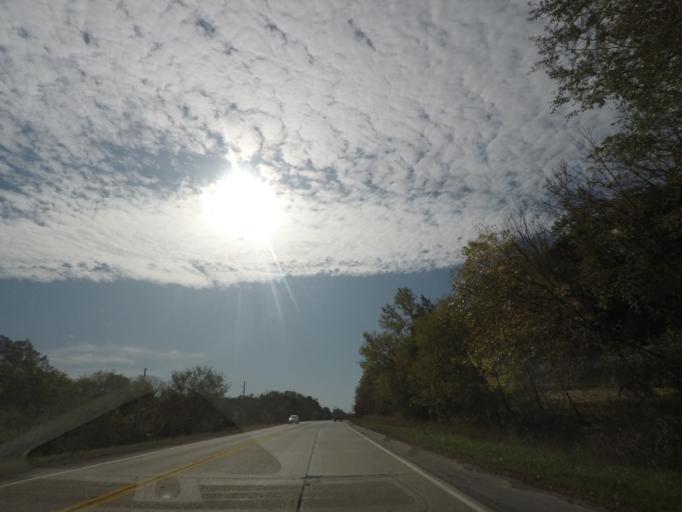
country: US
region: Iowa
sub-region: Story County
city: Ames
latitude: 42.0603
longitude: -93.6215
